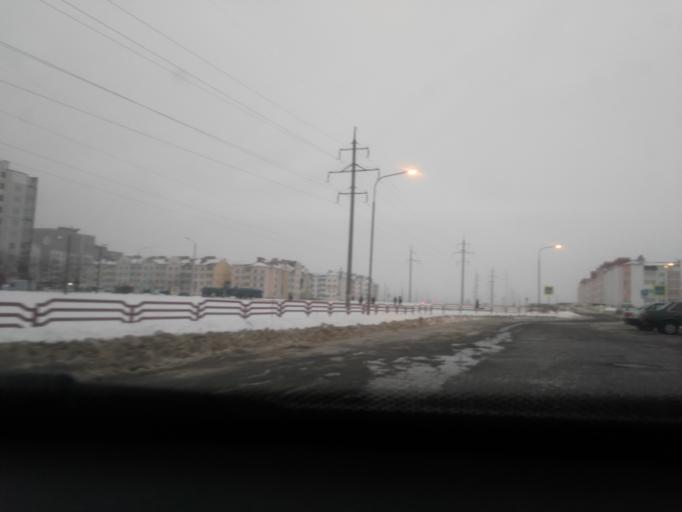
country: BY
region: Mogilev
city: Babruysk
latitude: 53.1990
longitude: 29.2223
